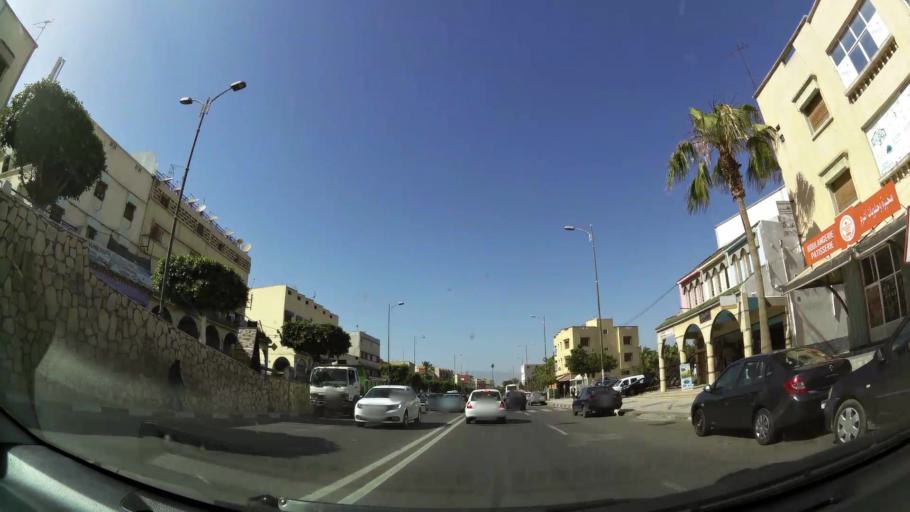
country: MA
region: Souss-Massa-Draa
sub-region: Inezgane-Ait Mellou
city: Inezgane
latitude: 30.3682
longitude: -9.5328
